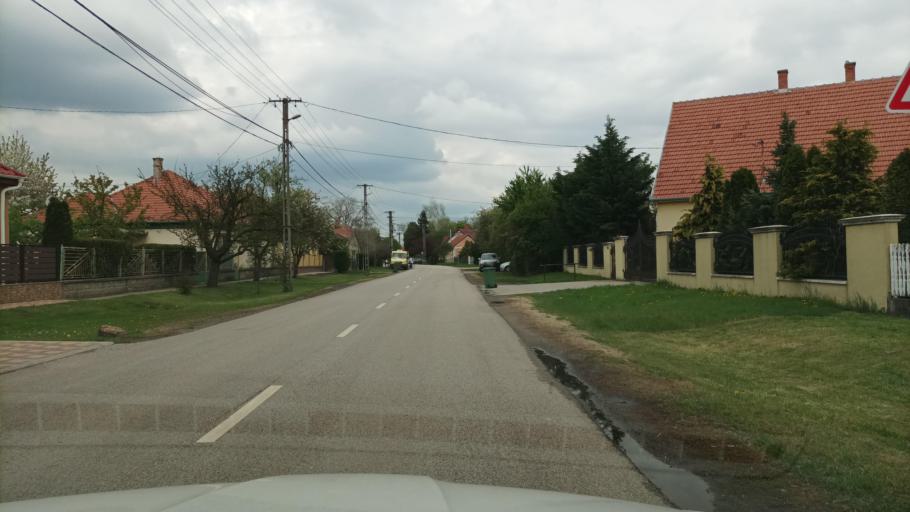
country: HU
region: Pest
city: Abony
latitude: 47.1840
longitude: 19.9985
